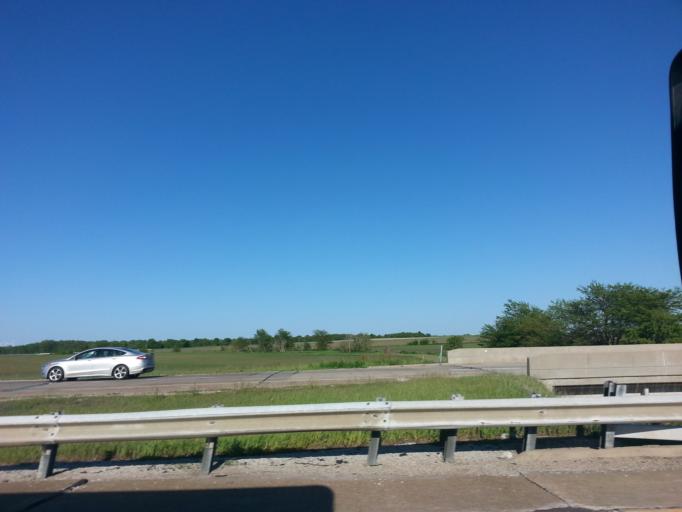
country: US
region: Illinois
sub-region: Woodford County
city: El Paso
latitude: 40.8005
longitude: -89.0357
